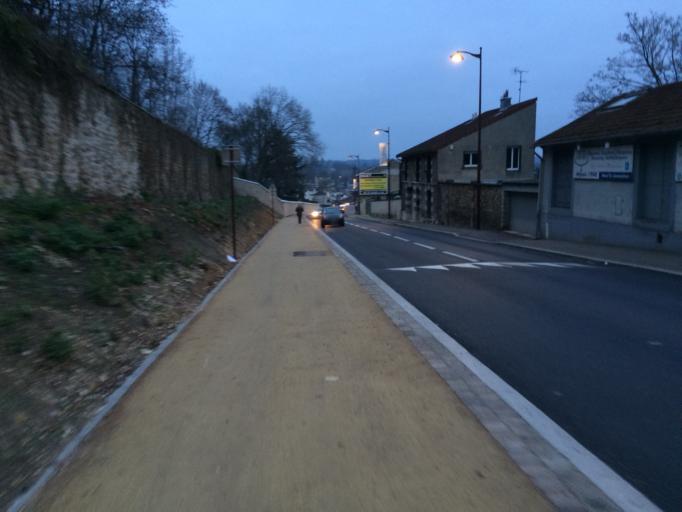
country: FR
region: Ile-de-France
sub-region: Departement des Yvelines
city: Versailles
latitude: 48.7918
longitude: 2.1360
